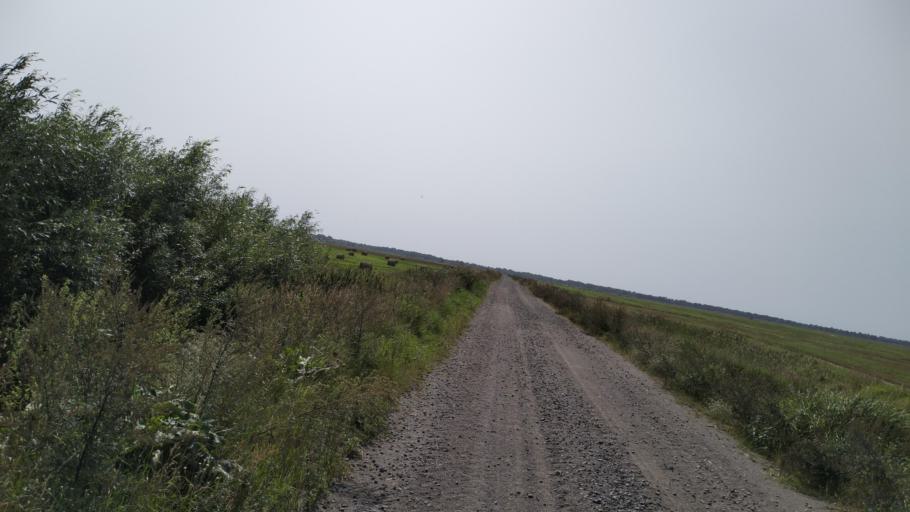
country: BY
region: Brest
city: Davyd-Haradok
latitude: 51.9891
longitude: 27.1758
